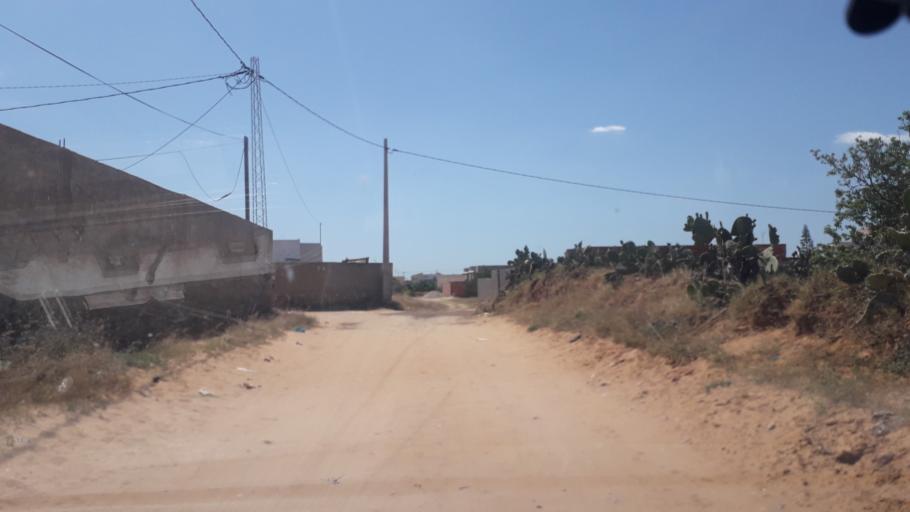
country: TN
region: Safaqis
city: Al Qarmadah
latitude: 34.8314
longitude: 10.7713
